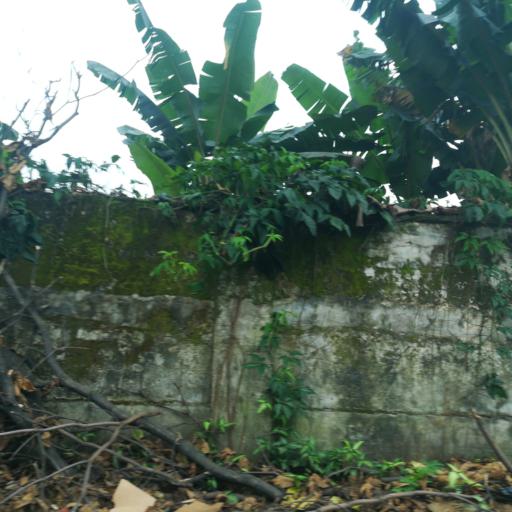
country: NG
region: Rivers
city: Port Harcourt
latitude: 4.7651
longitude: 7.0109
